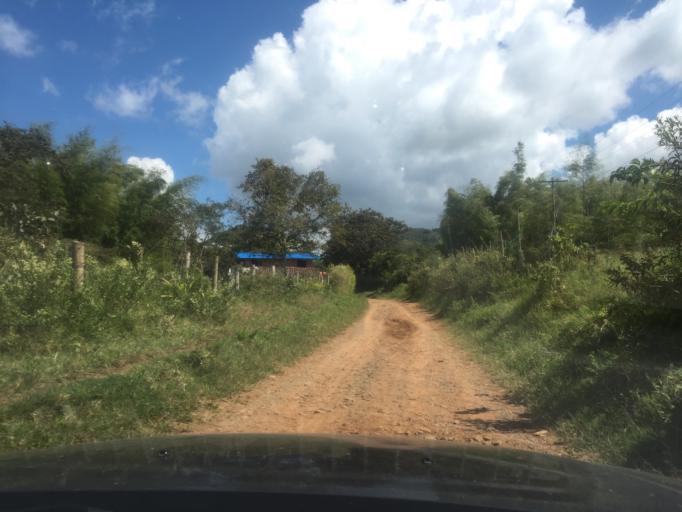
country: CO
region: Valle del Cauca
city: Yumbo
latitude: 3.6598
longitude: -76.5509
